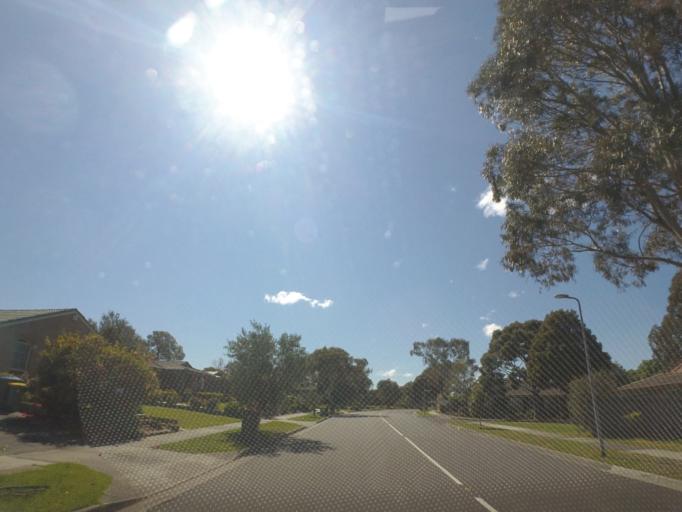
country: AU
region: Victoria
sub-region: Knox
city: Wantirna South
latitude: -37.8922
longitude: 145.2221
